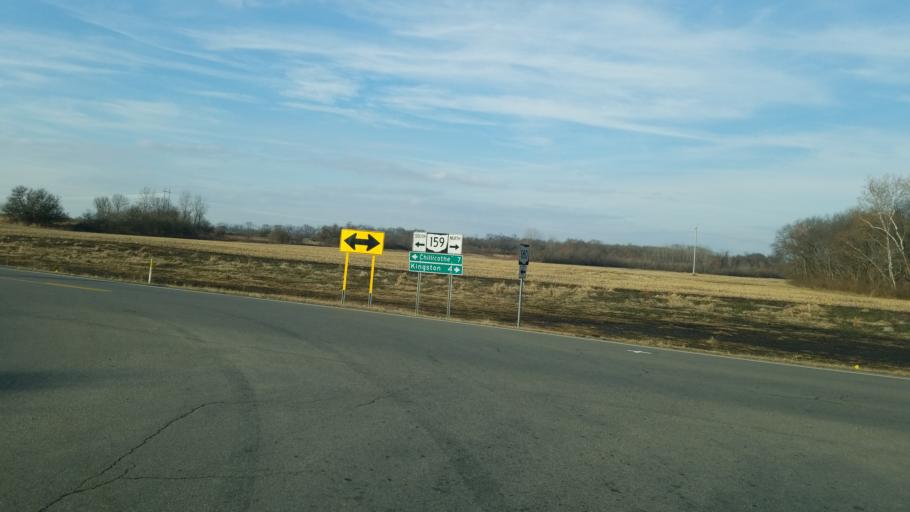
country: US
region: Ohio
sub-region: Ross County
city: Kingston
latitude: 39.4254
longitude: -82.9539
